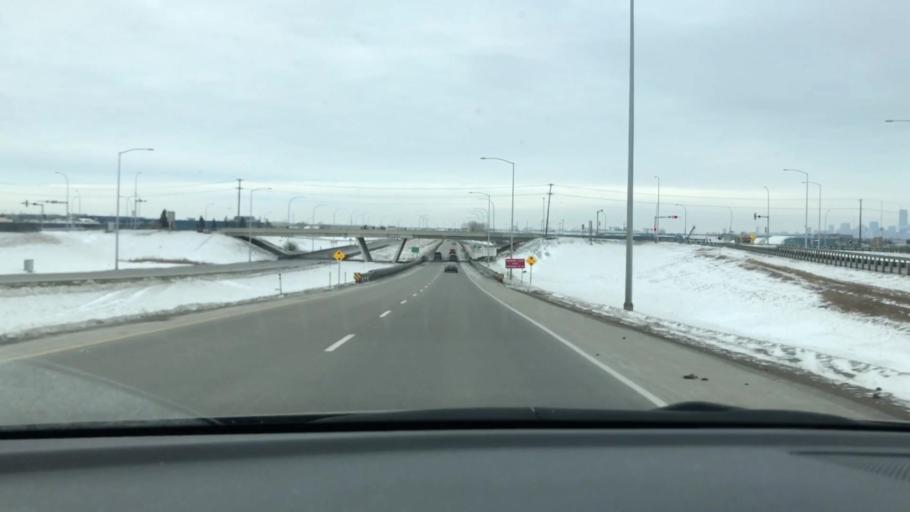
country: CA
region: Alberta
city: Sherwood Park
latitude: 53.5173
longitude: -113.3910
